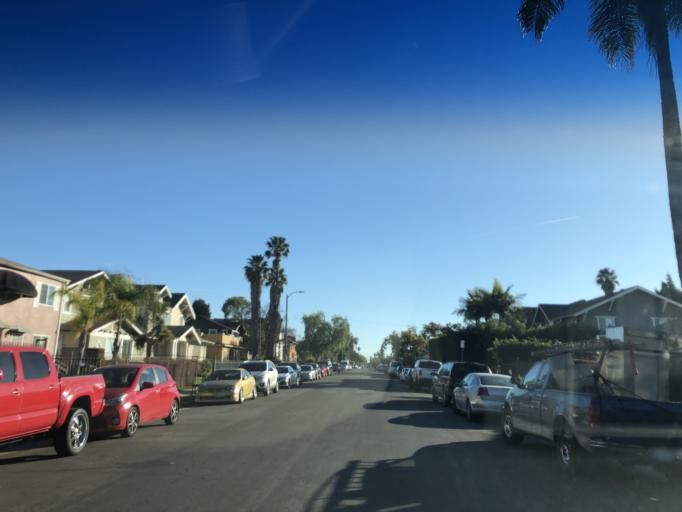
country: US
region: California
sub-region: Los Angeles County
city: Hollywood
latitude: 34.0466
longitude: -118.3226
